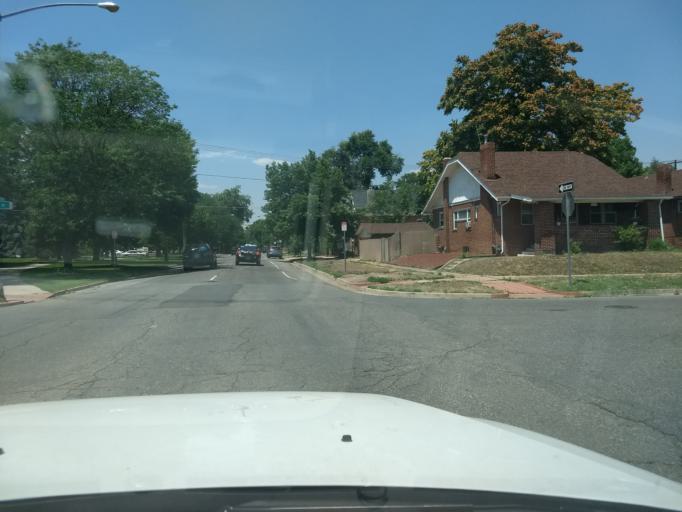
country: US
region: Colorado
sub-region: Denver County
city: Denver
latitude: 39.7620
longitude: -104.9646
